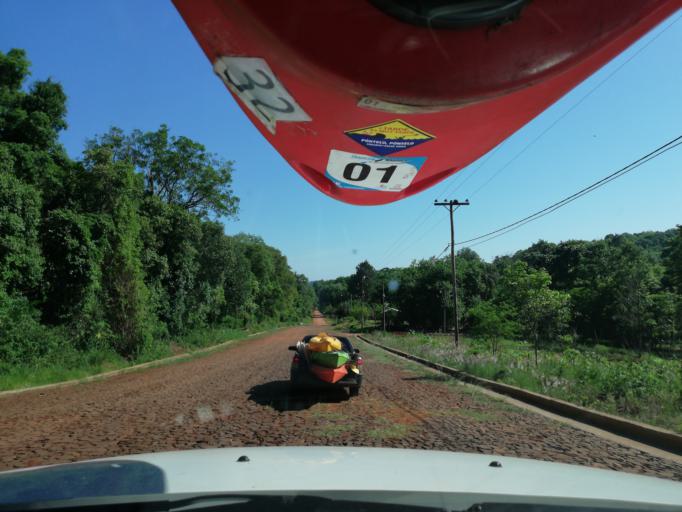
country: AR
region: Misiones
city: Puerto Leoni
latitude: -26.9820
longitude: -55.1648
